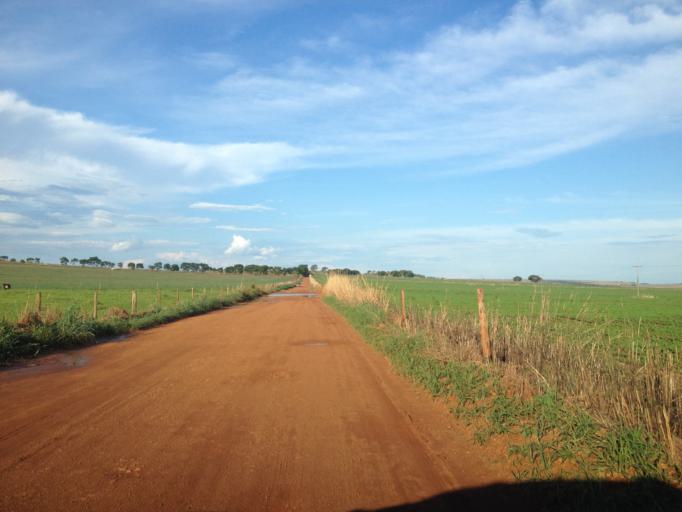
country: BR
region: Goias
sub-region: Abadiania
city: Abadiania
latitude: -15.9960
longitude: -48.5419
